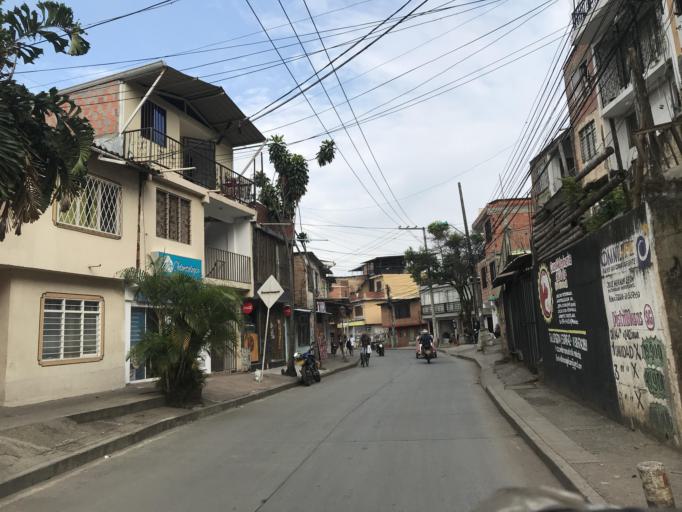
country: CO
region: Valle del Cauca
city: Cali
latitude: 3.3743
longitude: -76.5497
